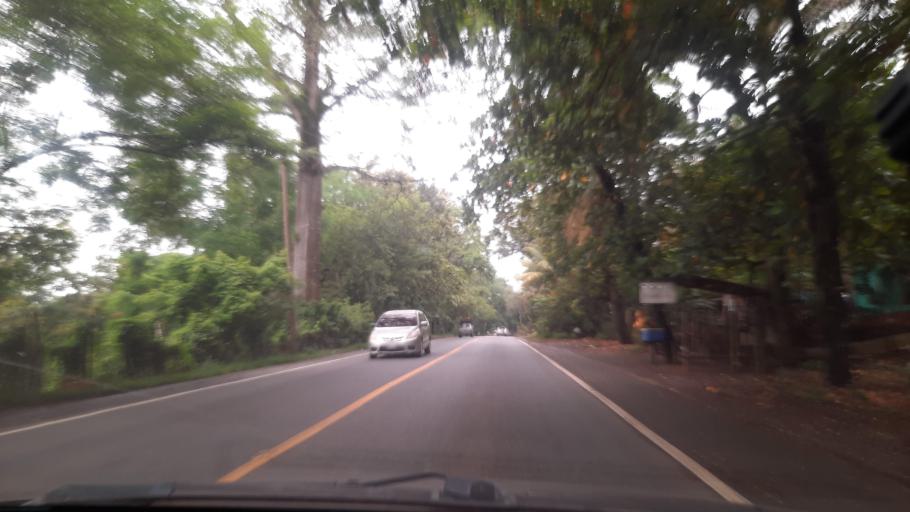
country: GT
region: Izabal
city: Morales
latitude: 15.4311
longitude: -88.9699
